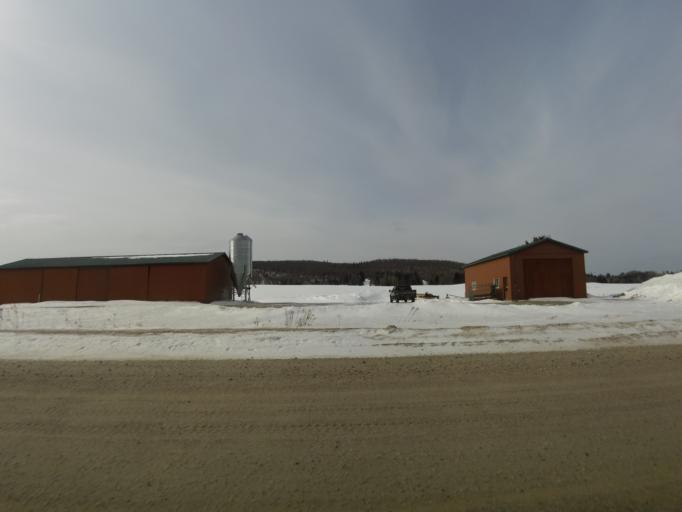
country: CA
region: Quebec
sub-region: Laurentides
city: Ferme-Neuve
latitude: 46.9330
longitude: -75.3547
